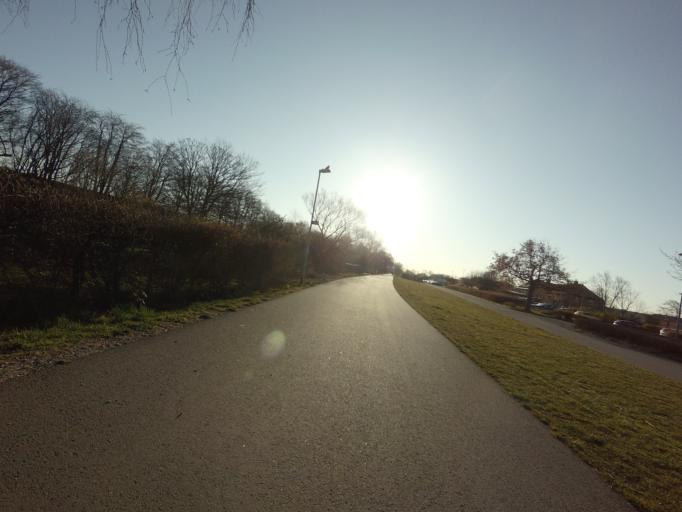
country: SE
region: Skane
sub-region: Hoganas Kommun
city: Hoganas
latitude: 56.2025
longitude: 12.5572
